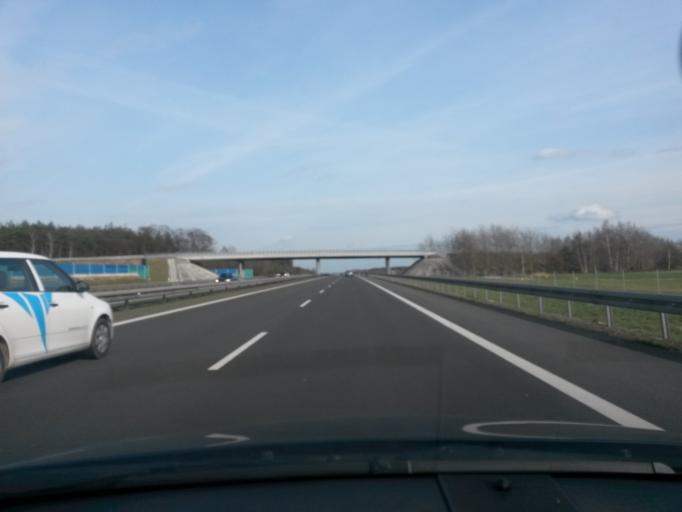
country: PL
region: Greater Poland Voivodeship
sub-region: Powiat koninski
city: Stare Miasto
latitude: 52.1705
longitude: 18.1631
